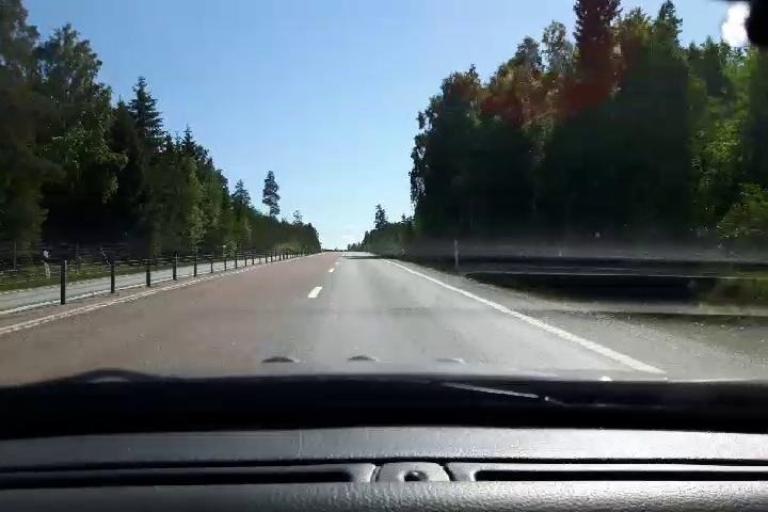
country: SE
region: Gaevleborg
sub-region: Soderhamns Kommun
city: Ljusne
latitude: 61.1360
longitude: 17.0234
